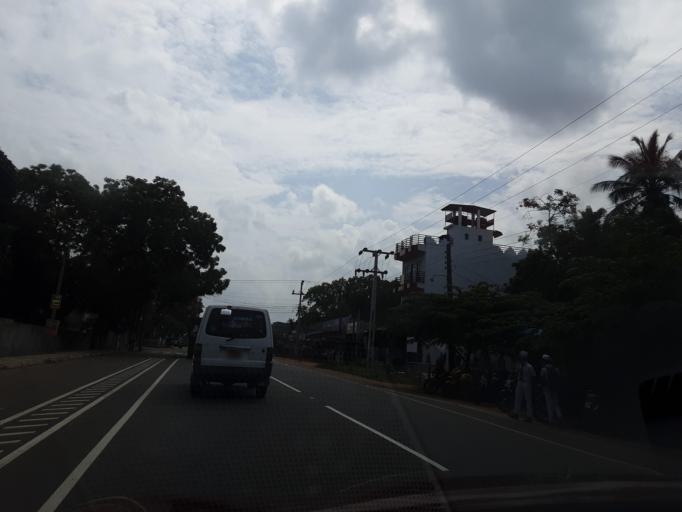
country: LK
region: North Central
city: Anuradhapura
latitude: 8.4712
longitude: 80.5126
